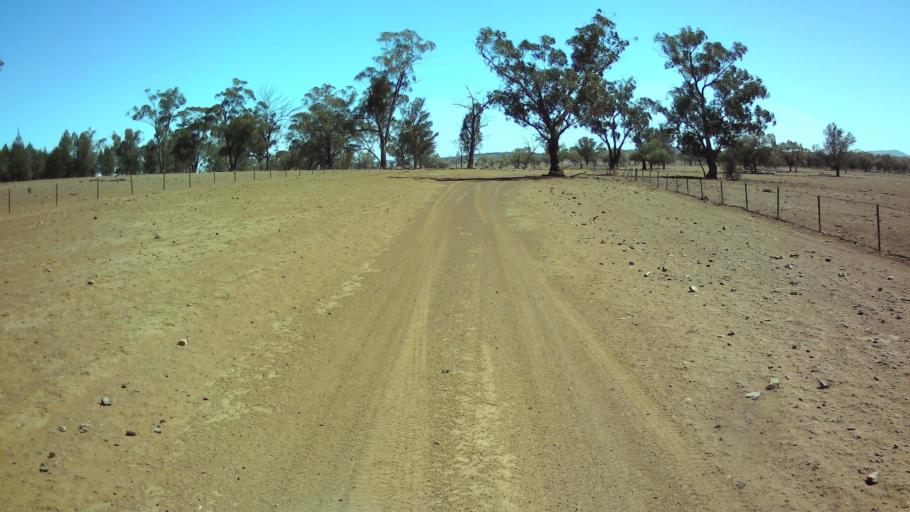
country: AU
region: New South Wales
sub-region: Forbes
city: Forbes
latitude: -33.7308
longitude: 147.6656
